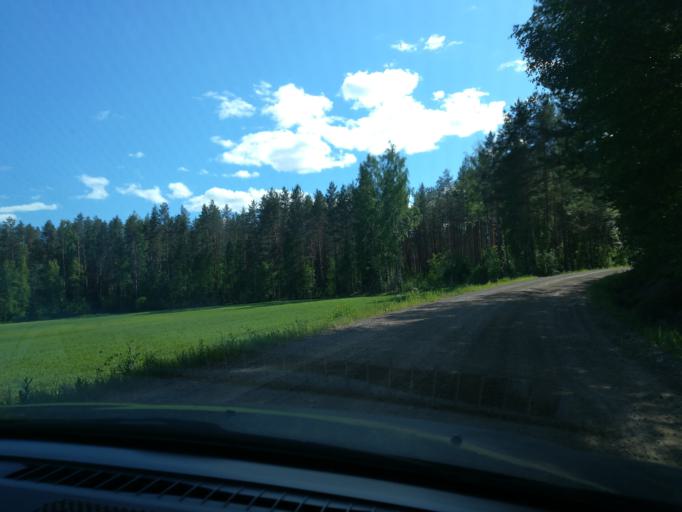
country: FI
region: Southern Savonia
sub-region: Mikkeli
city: Puumala
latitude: 61.6570
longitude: 28.1266
